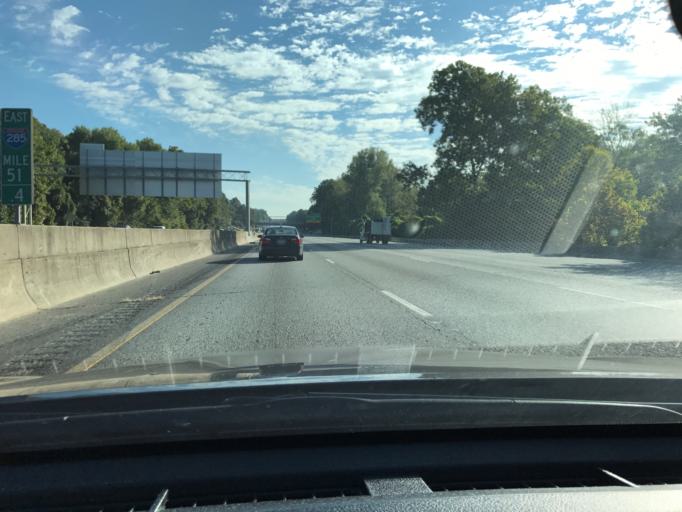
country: US
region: Georgia
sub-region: DeKalb County
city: Gresham Park
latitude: 33.6798
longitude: -84.3155
